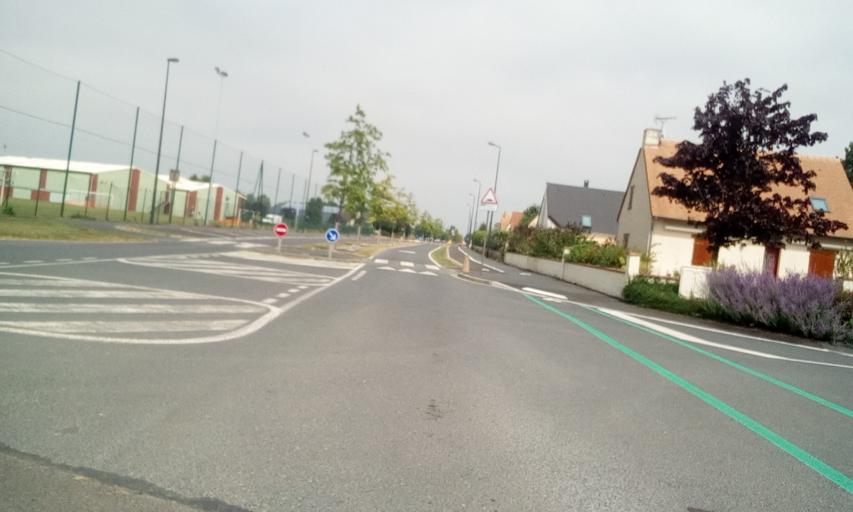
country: FR
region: Lower Normandy
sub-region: Departement du Calvados
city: Douvres-la-Delivrande
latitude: 49.2956
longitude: -0.3903
